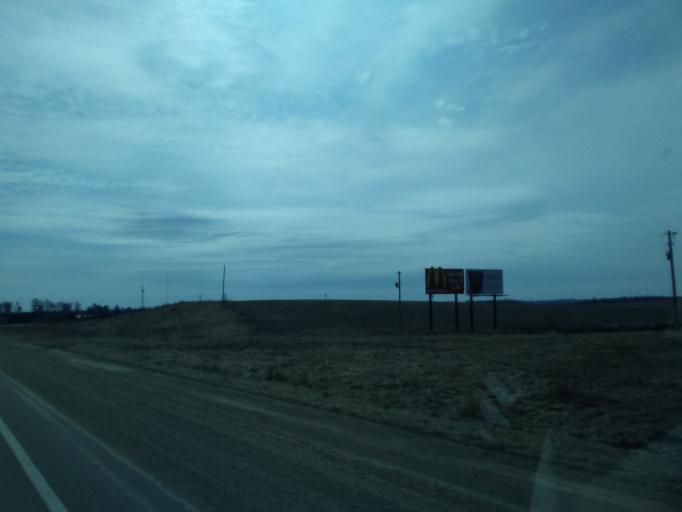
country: US
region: Iowa
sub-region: Winneshiek County
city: Decorah
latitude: 43.3592
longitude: -91.8045
